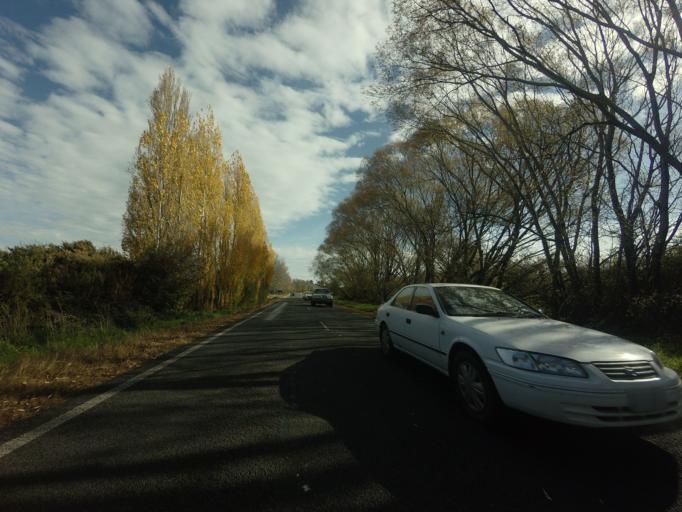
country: AU
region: Tasmania
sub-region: Meander Valley
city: Westbury
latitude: -41.5281
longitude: 146.8003
